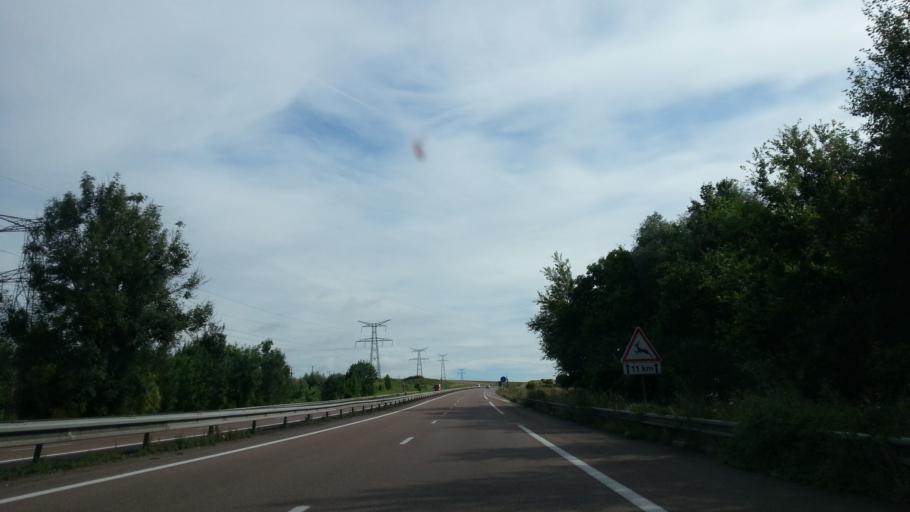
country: FR
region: Champagne-Ardenne
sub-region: Departement de la Marne
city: Jonchery-sur-Vesle
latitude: 49.2236
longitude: 3.8187
